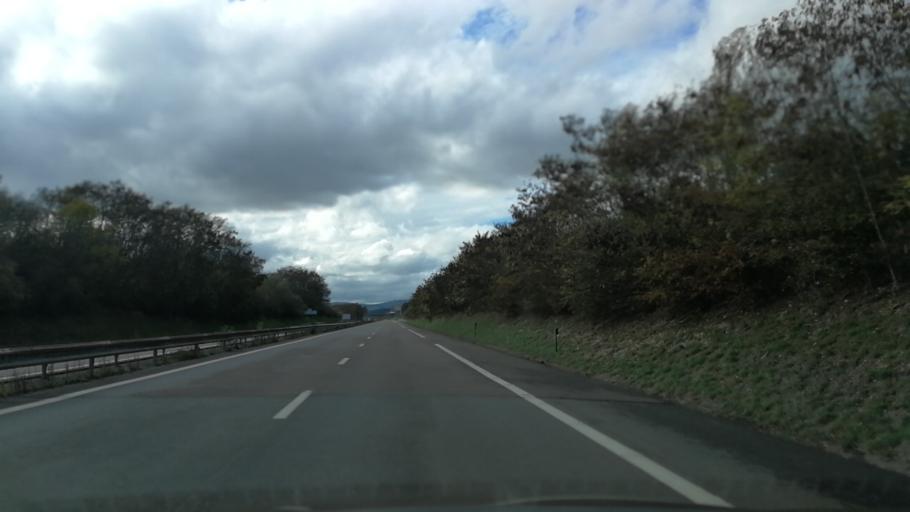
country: FR
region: Bourgogne
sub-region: Departement de la Cote-d'Or
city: Fleurey-sur-Ouche
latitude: 47.3084
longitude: 4.8693
